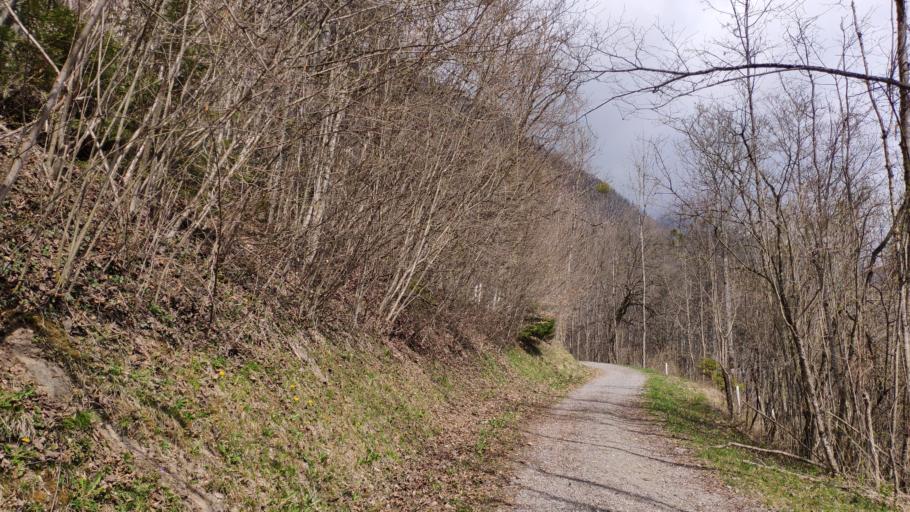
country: CH
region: Bern
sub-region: Interlaken-Oberhasli District
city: Brienz
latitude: 46.7512
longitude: 7.9811
